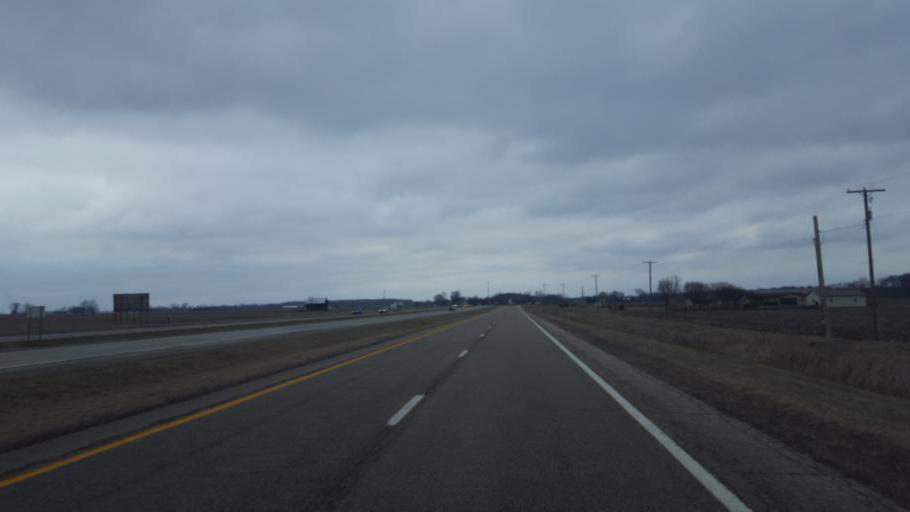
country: US
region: Ohio
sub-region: Marion County
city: Prospect
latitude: 40.4195
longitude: -83.0740
